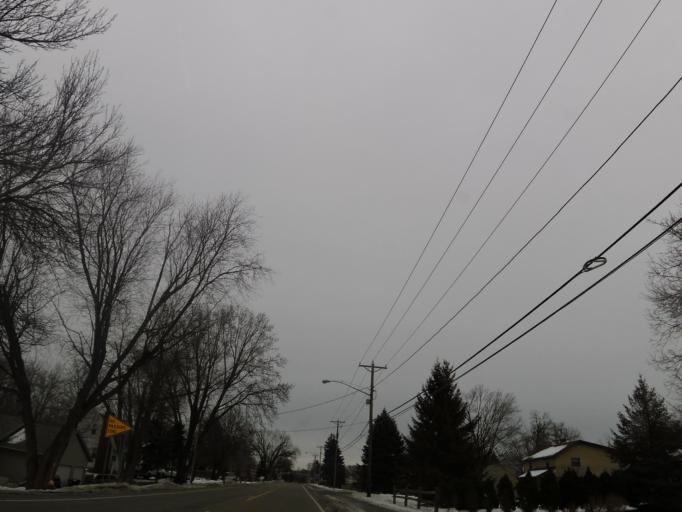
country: US
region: Minnesota
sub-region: Ramsey County
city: Maplewood
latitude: 44.9740
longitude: -92.9883
